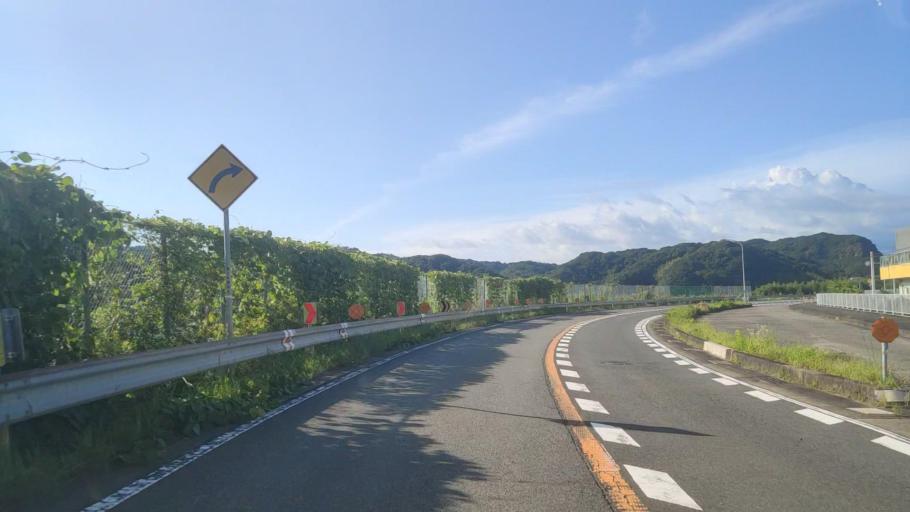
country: JP
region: Wakayama
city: Tanabe
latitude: 33.6621
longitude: 135.3989
